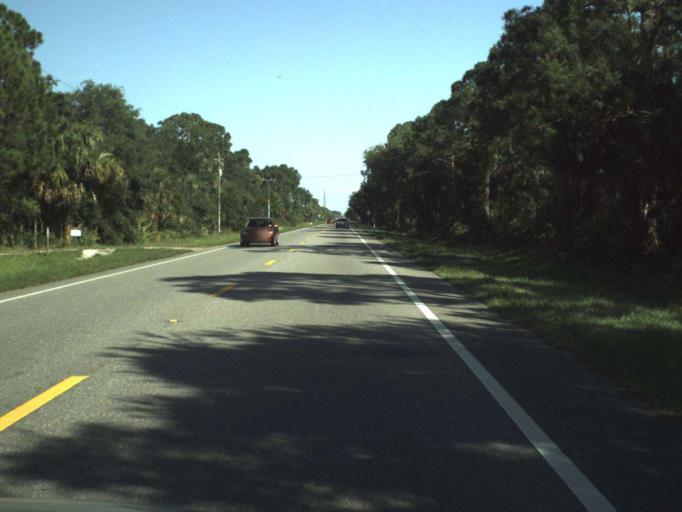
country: US
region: Florida
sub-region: Seminole County
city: Geneva
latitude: 28.7685
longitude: -81.1543
